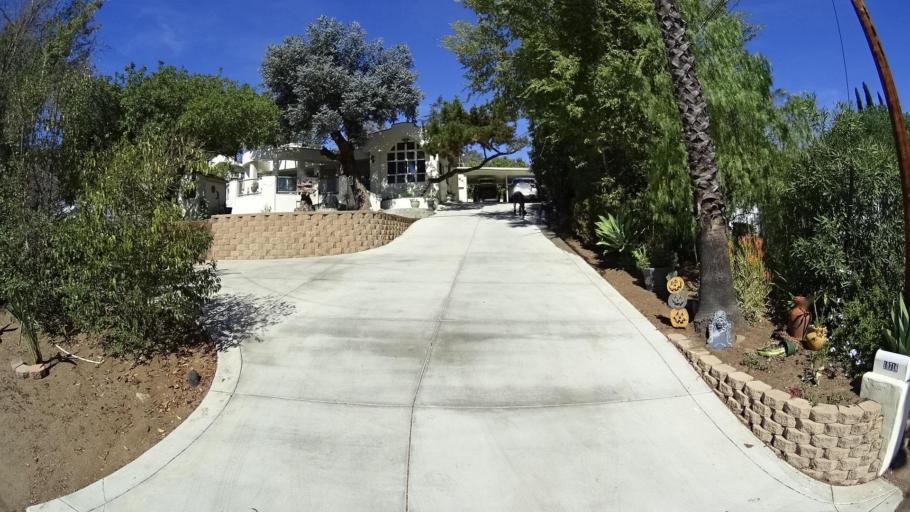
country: US
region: California
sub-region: San Diego County
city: Casa de Oro-Mount Helix
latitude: 32.7573
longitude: -116.9636
